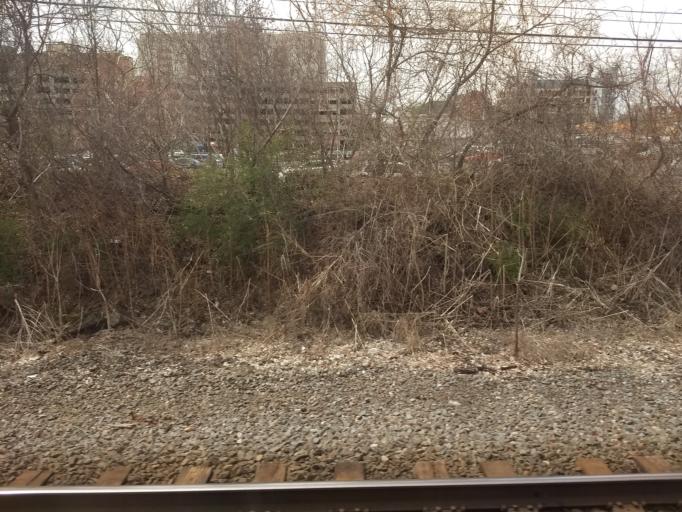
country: US
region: Pennsylvania
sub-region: Dauphin County
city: Harrisburg
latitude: 40.2736
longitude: -76.8833
